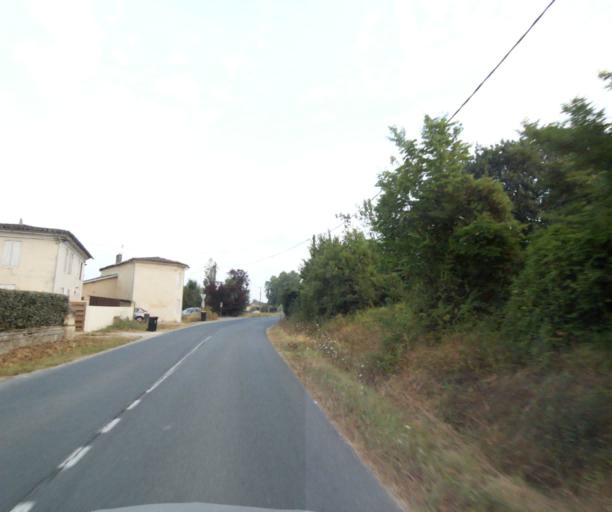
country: FR
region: Aquitaine
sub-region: Departement de la Gironde
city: La Sauve
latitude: 44.7572
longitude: -0.3288
